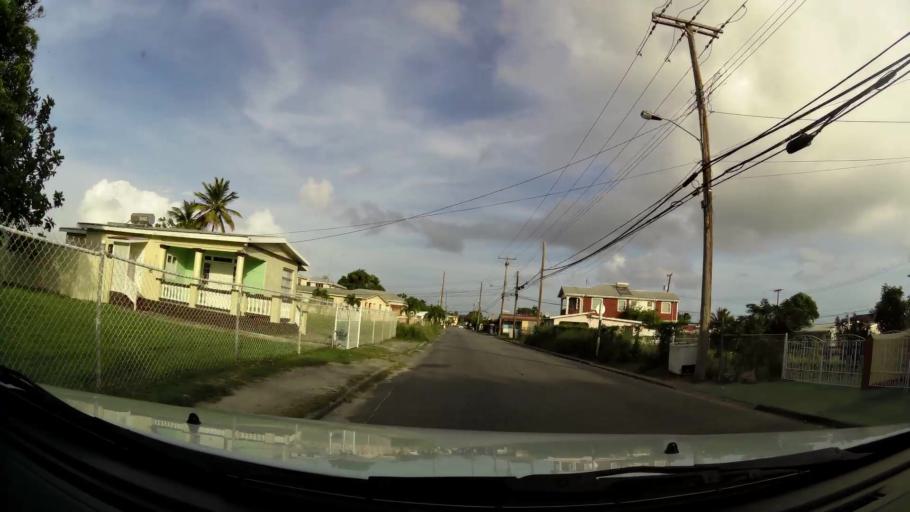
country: BB
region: Christ Church
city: Oistins
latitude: 13.0586
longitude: -59.5313
